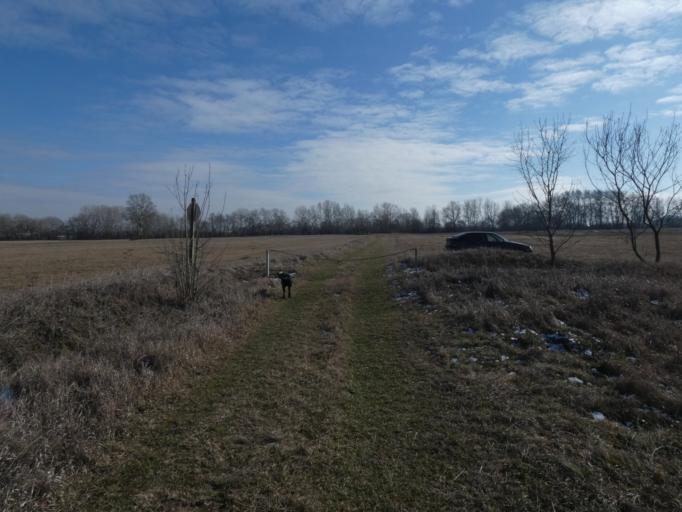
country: HU
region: Pest
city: Dabas
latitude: 47.1741
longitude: 19.2941
